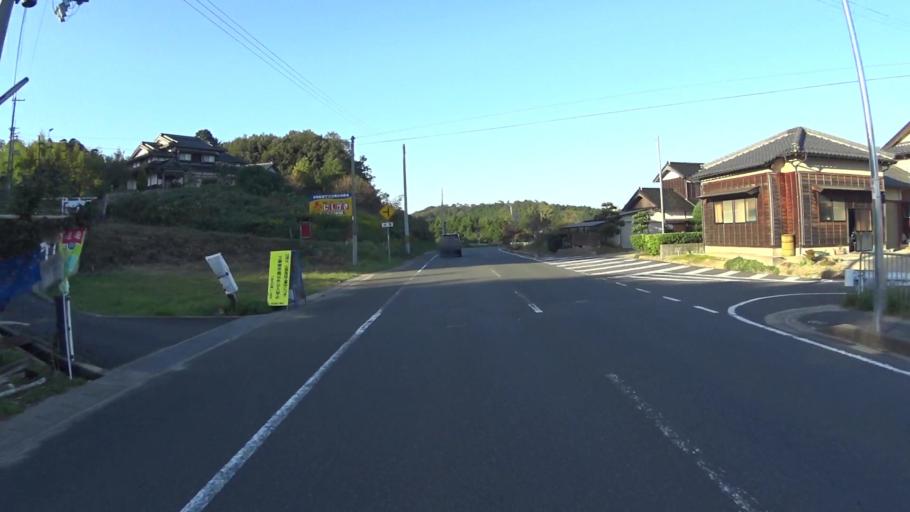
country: JP
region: Hyogo
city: Toyooka
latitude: 35.6136
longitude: 134.9192
